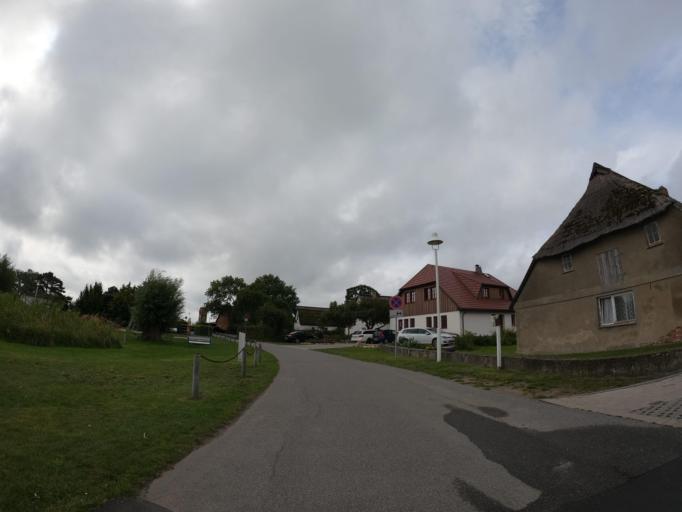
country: DE
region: Mecklenburg-Vorpommern
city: Ostseebad Gohren
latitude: 54.2819
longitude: 13.6937
